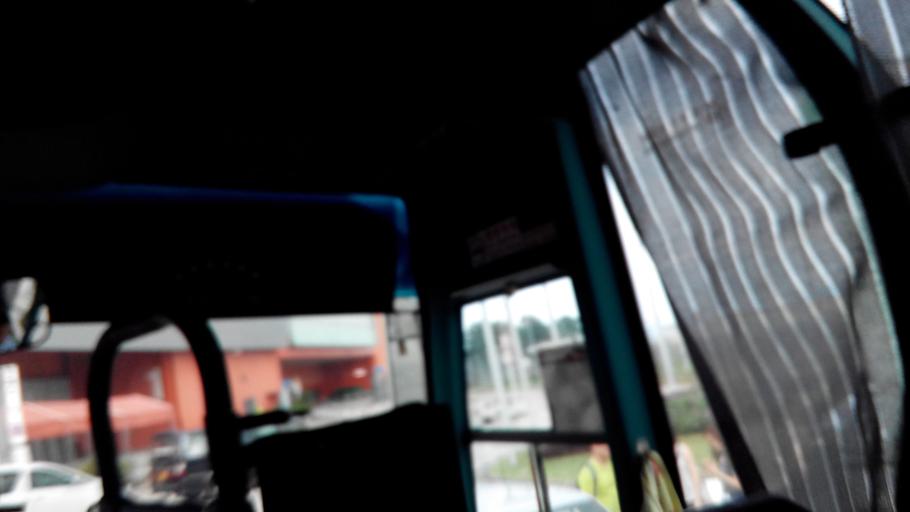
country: HK
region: Tuen Mun
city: Tuen Mun
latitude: 22.3206
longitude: 113.9444
